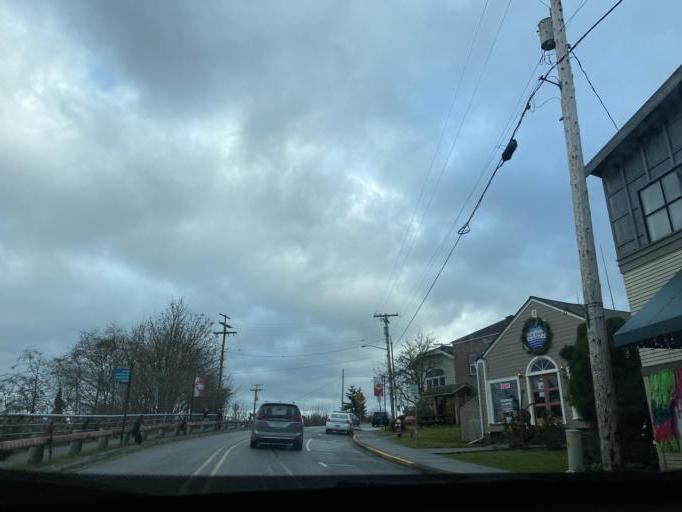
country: US
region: Washington
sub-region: Island County
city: Langley
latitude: 48.0405
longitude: -122.4072
